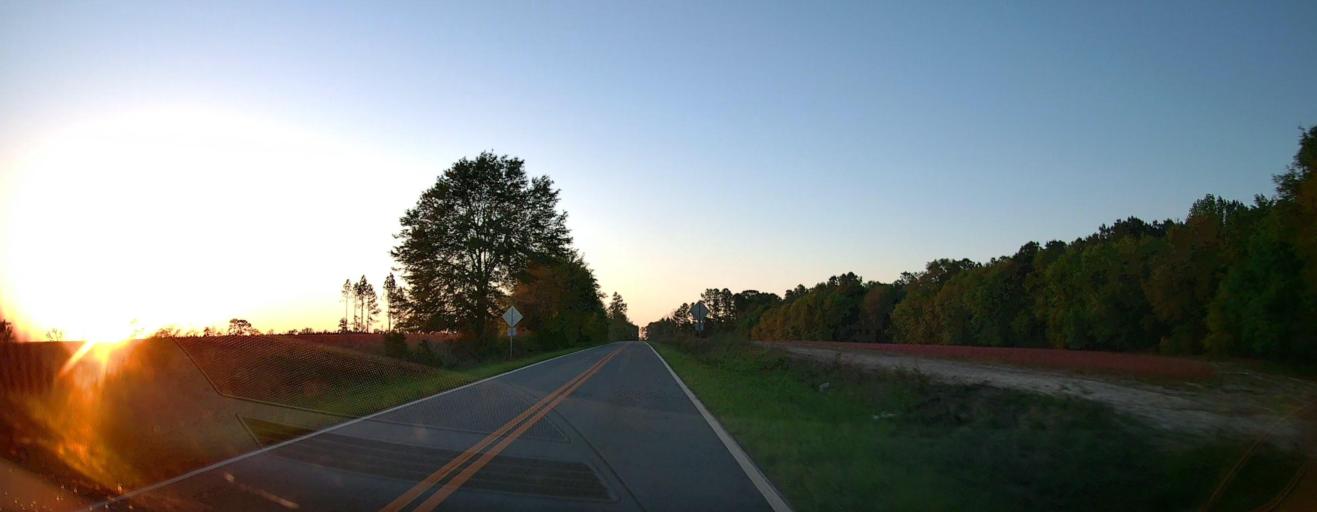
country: US
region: Georgia
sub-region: Wilcox County
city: Rochelle
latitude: 31.8029
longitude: -83.4546
